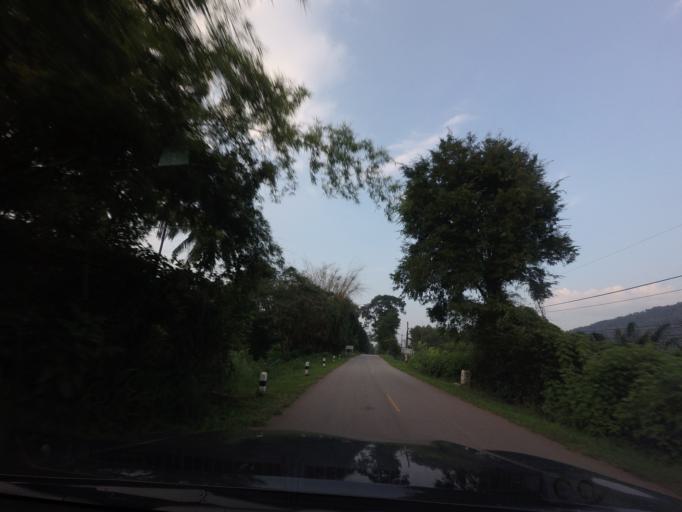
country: TH
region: Loei
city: Na Haeo
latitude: 17.4197
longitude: 101.0479
